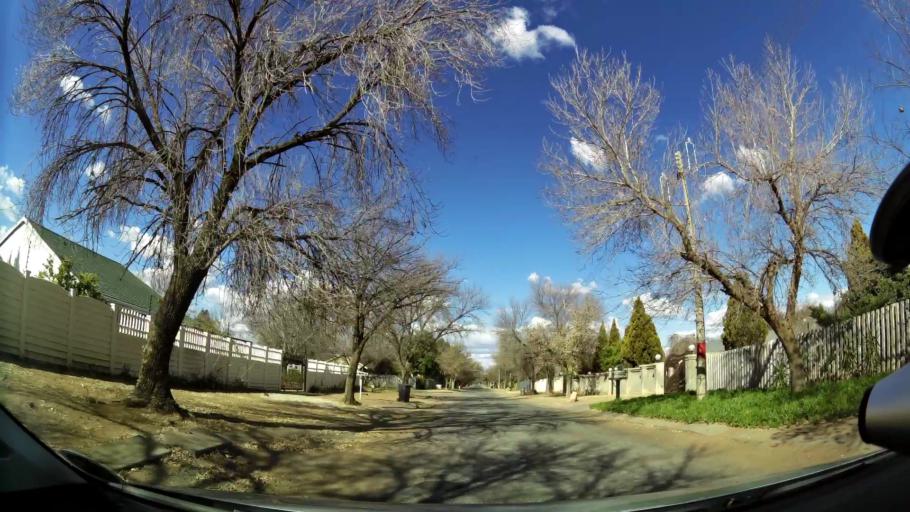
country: ZA
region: North-West
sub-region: Dr Kenneth Kaunda District Municipality
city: Klerksdorp
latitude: -26.8420
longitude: 26.6482
